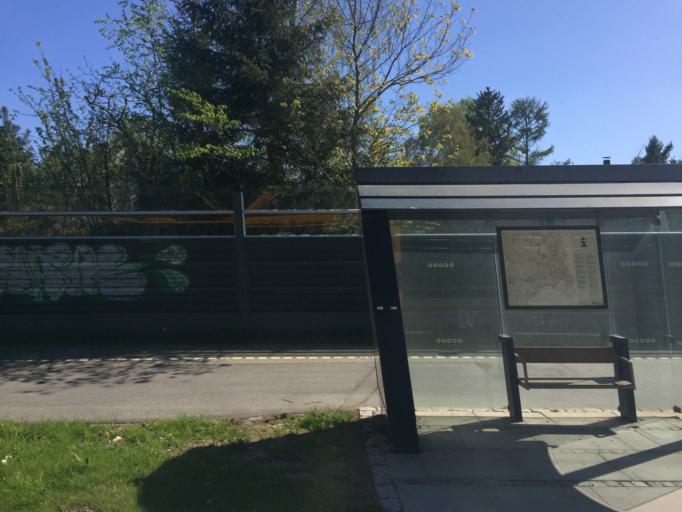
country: DK
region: Capital Region
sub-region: Herlev Kommune
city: Herlev
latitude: 55.7577
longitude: 12.4234
